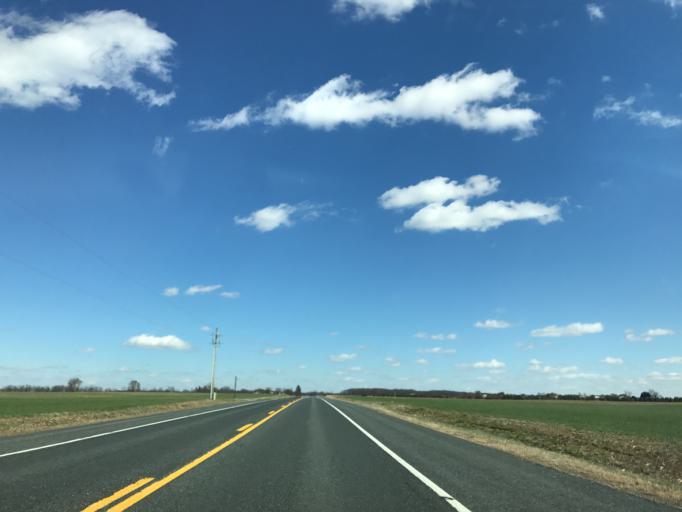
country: US
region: Maryland
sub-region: Queen Anne's County
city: Kingstown
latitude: 39.1993
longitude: -76.0262
